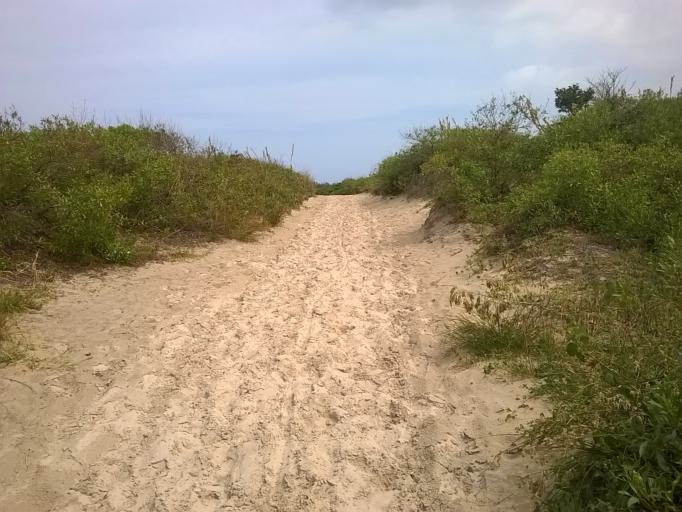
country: BR
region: Santa Catarina
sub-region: Florianopolis
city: Rio Tavares
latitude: -27.6915
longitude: -48.4837
